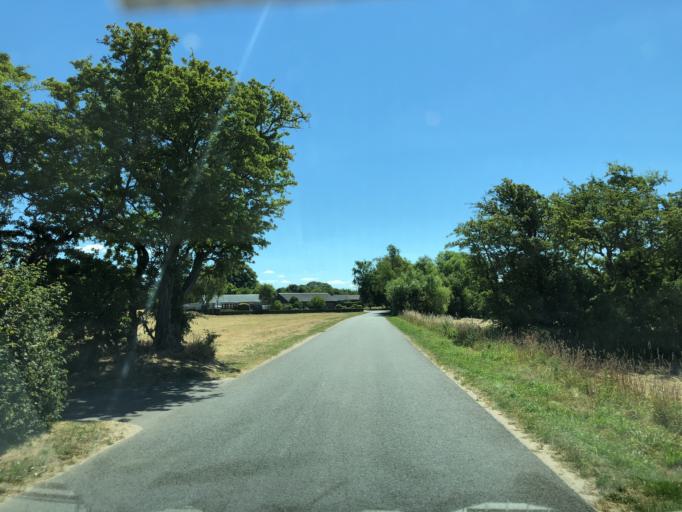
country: DK
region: Central Jutland
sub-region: Viborg Kommune
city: Viborg
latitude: 56.5371
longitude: 9.4709
